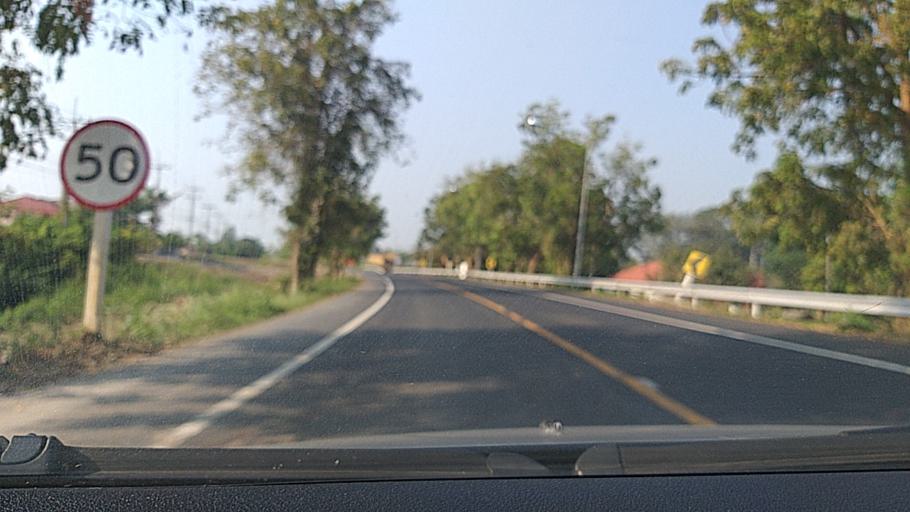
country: TH
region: Sing Buri
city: Phrom Buri
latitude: 14.7663
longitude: 100.4403
